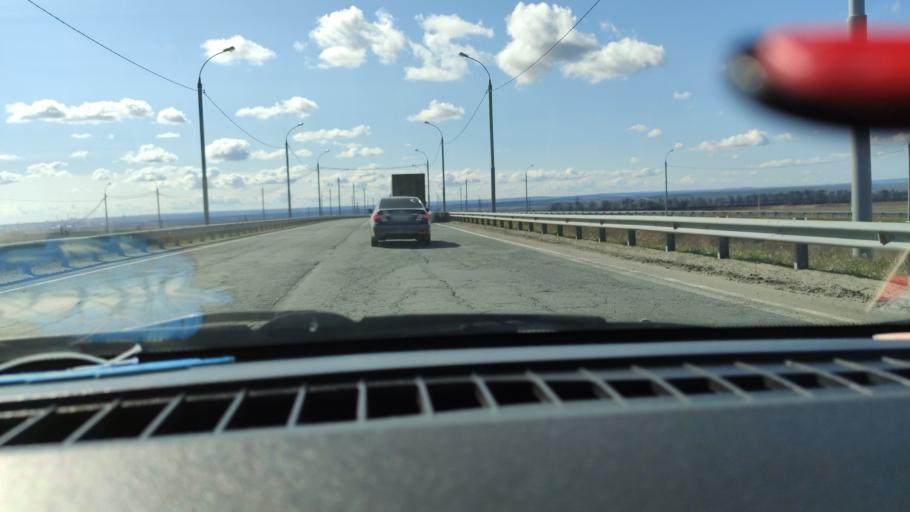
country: RU
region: Samara
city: Varlamovo
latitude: 53.1921
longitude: 48.2924
